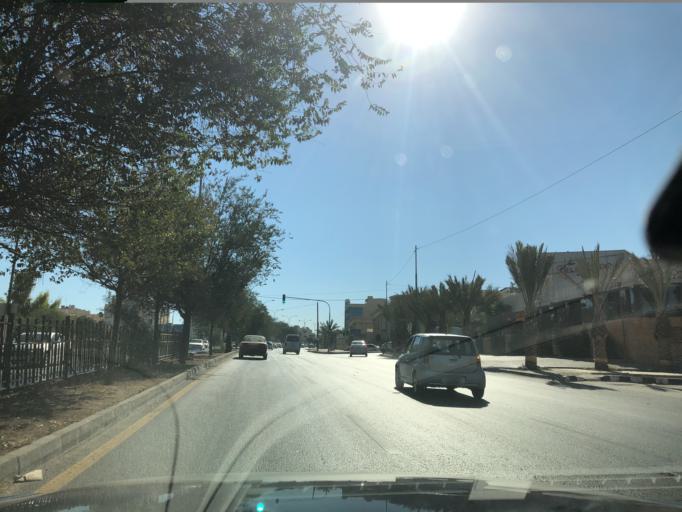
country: JO
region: Amman
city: Al Jubayhah
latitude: 31.9736
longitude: 35.8706
